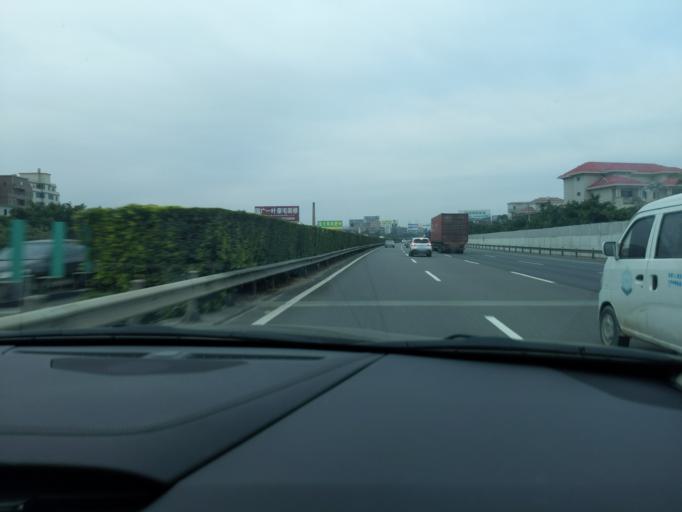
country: CN
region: Fujian
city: Anhai
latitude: 24.7405
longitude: 118.4248
